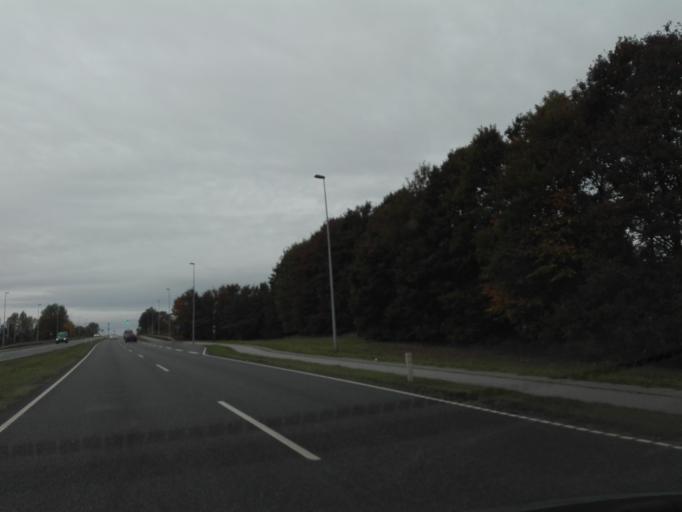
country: DK
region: Central Jutland
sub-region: Arhus Kommune
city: Stavtrup
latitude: 56.1191
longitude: 10.1428
